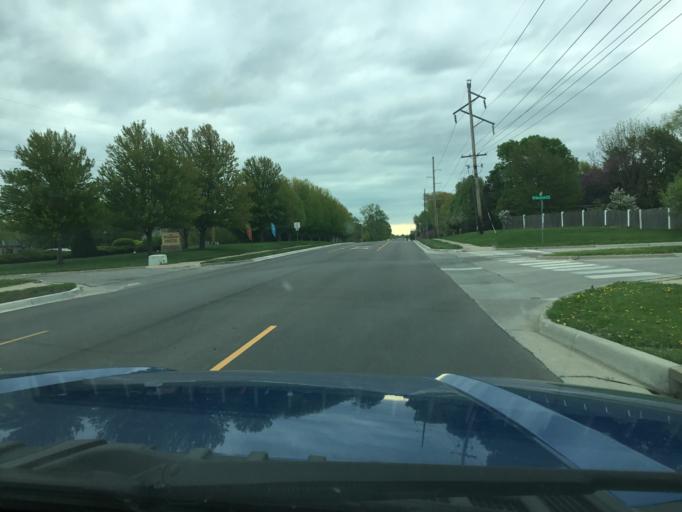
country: US
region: Kansas
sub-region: Douglas County
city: Lawrence
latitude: 38.9861
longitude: -95.2767
